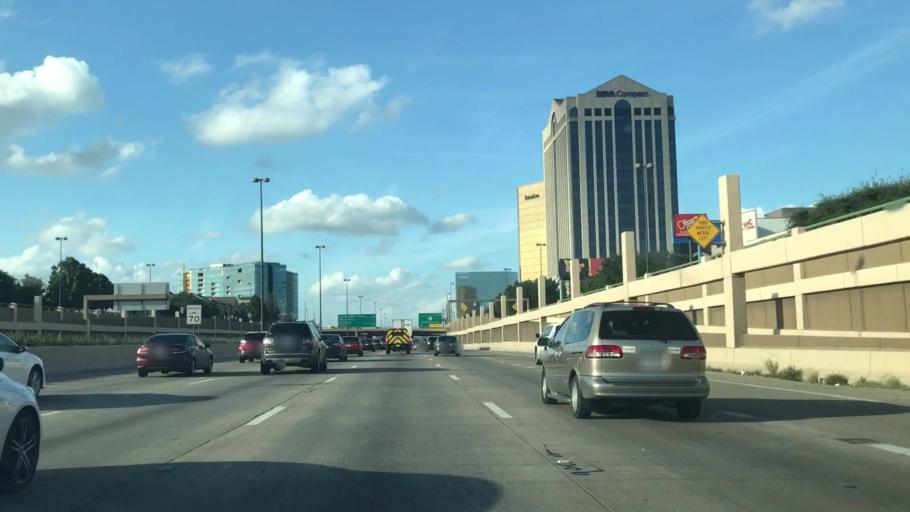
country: US
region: Texas
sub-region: Dallas County
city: University Park
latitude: 32.8579
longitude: -96.7702
